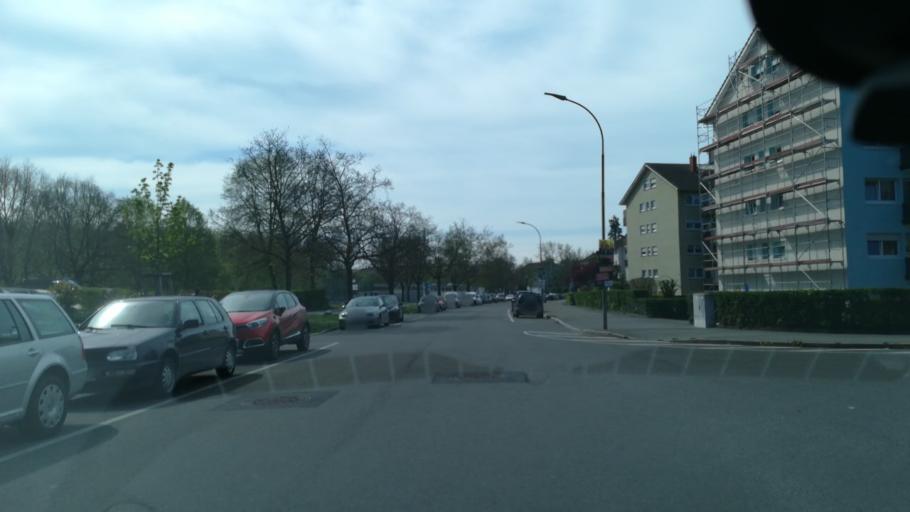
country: DE
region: Baden-Wuerttemberg
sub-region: Freiburg Region
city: Singen
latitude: 47.7735
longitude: 8.8453
